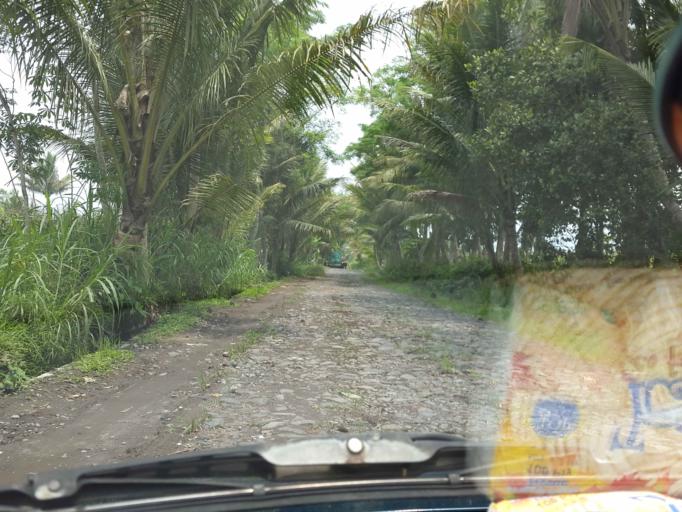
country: ID
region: Central Java
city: Muntilan
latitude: -7.5973
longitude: 110.3165
